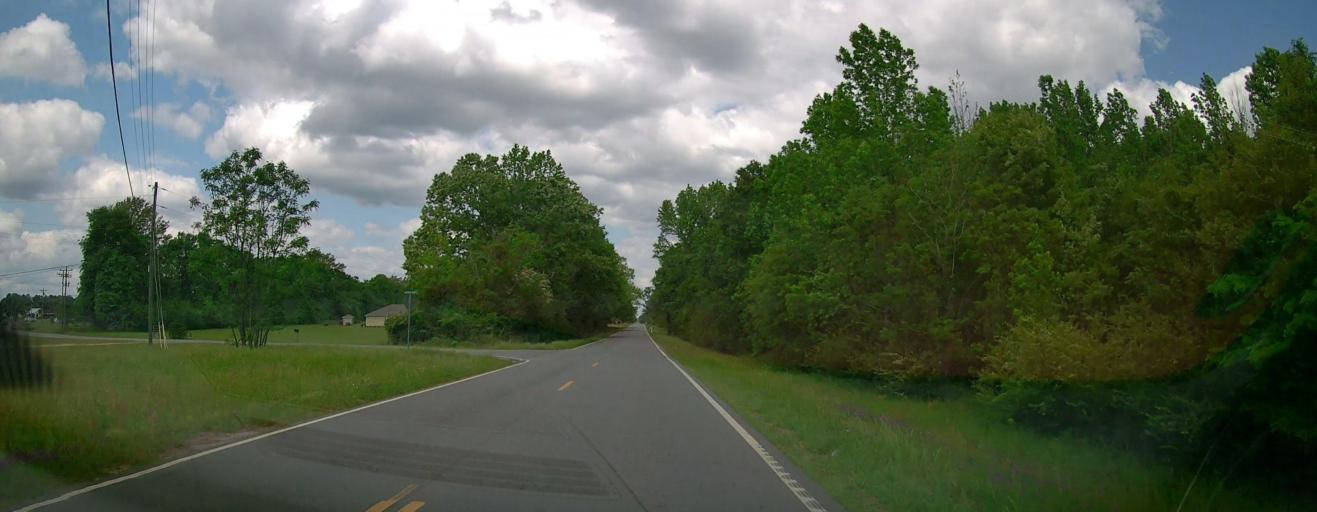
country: US
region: Georgia
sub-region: Laurens County
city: Dublin
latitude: 32.5999
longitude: -82.9563
